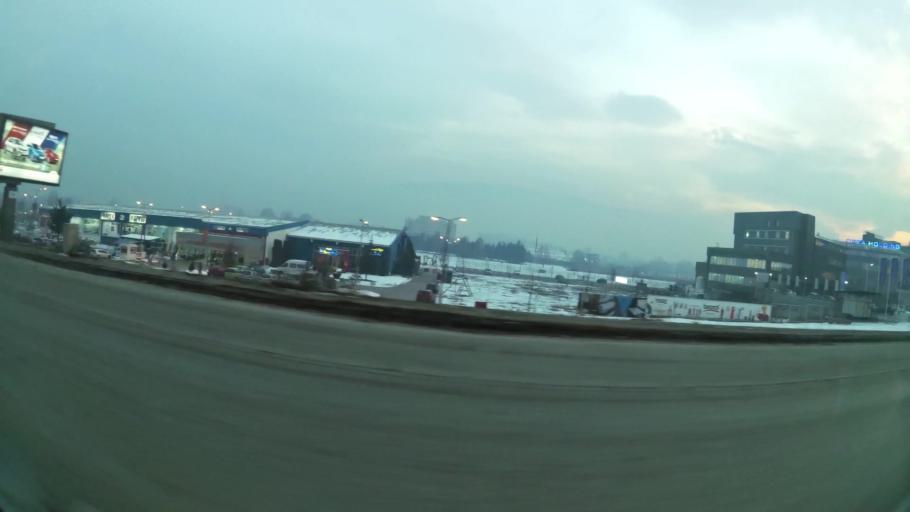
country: MK
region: Karpos
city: Skopje
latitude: 42.0147
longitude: 21.4056
